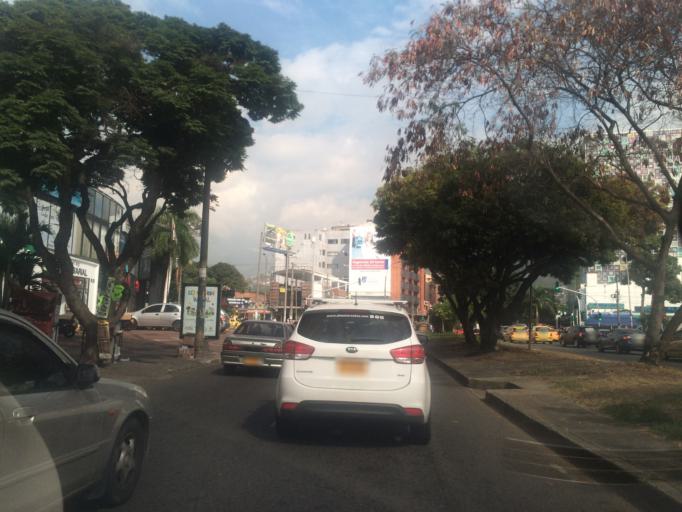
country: CO
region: Valle del Cauca
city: Cali
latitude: 3.4218
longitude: -76.5411
